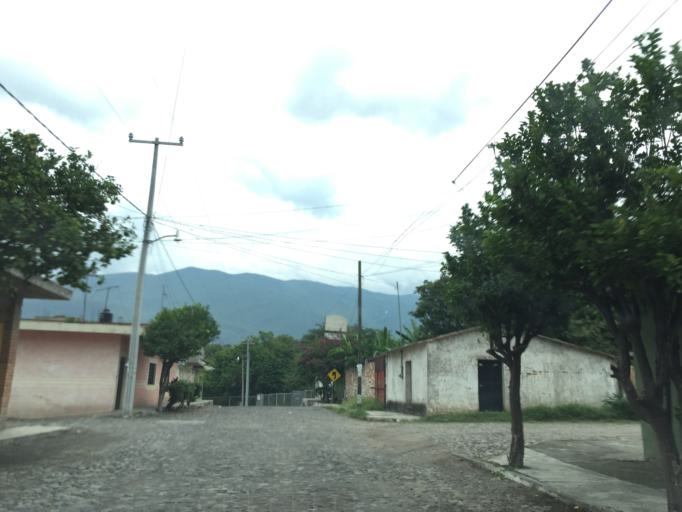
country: MX
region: Colima
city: Comala
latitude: 19.3717
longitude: -103.8000
